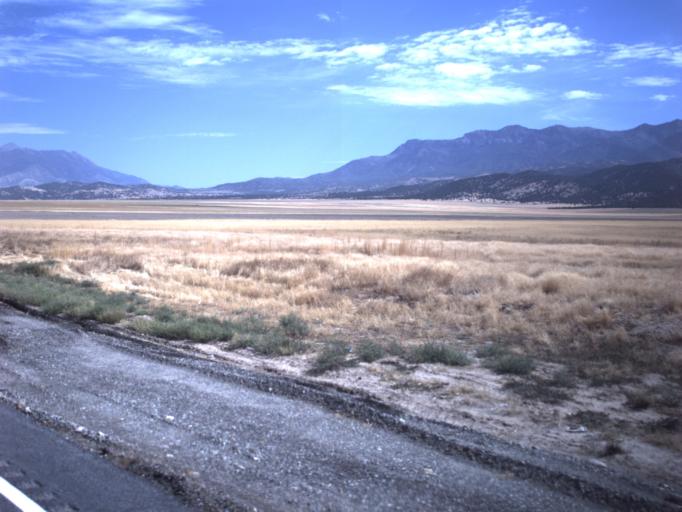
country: US
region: Utah
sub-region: Juab County
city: Nephi
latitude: 39.5853
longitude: -111.8617
